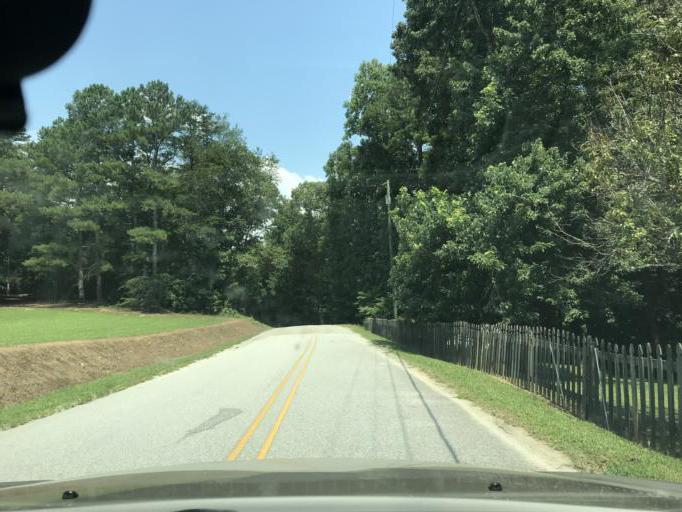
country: US
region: Georgia
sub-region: Dawson County
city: Dawsonville
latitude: 34.3480
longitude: -84.0887
